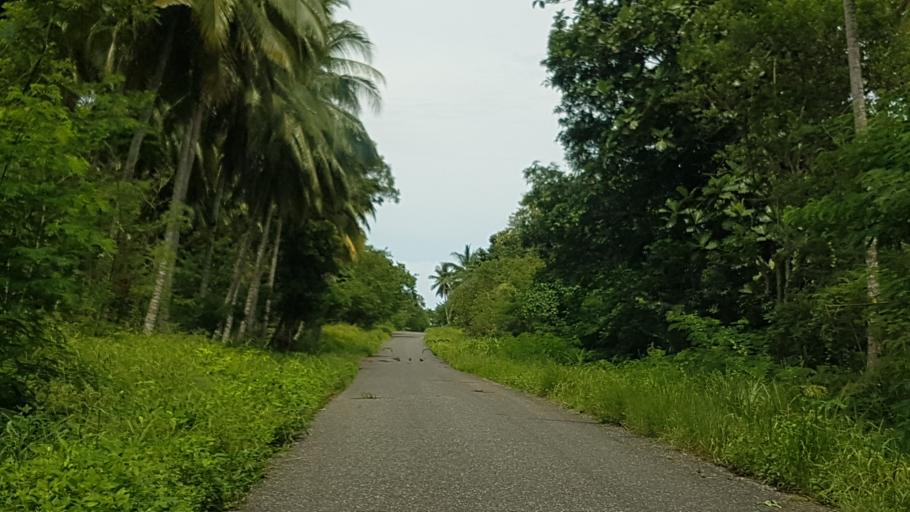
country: PG
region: Madang
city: Madang
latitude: -4.5947
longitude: 145.5423
